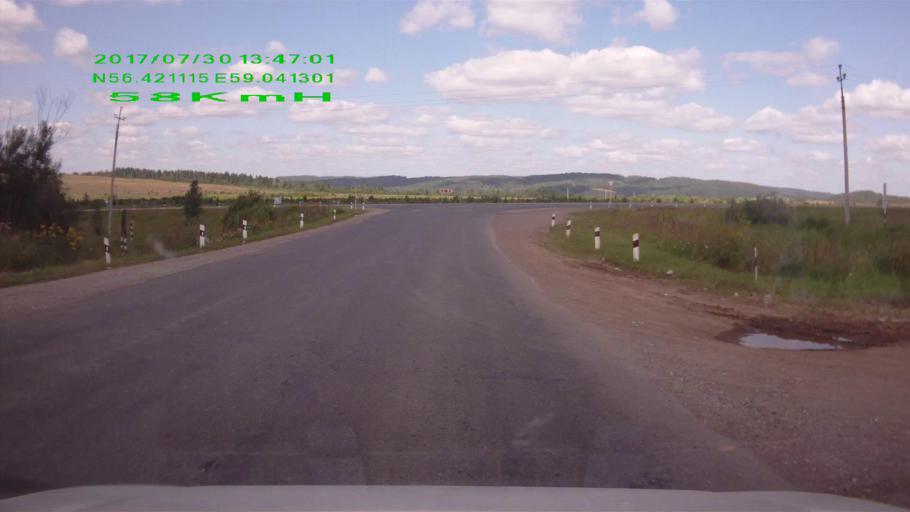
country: RU
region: Sverdlovsk
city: Mikhaylovsk
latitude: 56.4214
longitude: 59.0413
